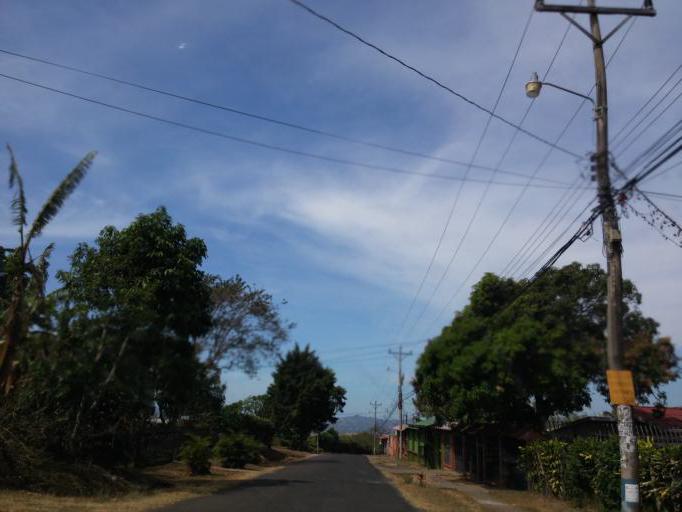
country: CR
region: Alajuela
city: Alajuela
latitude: 10.0435
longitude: -84.2324
